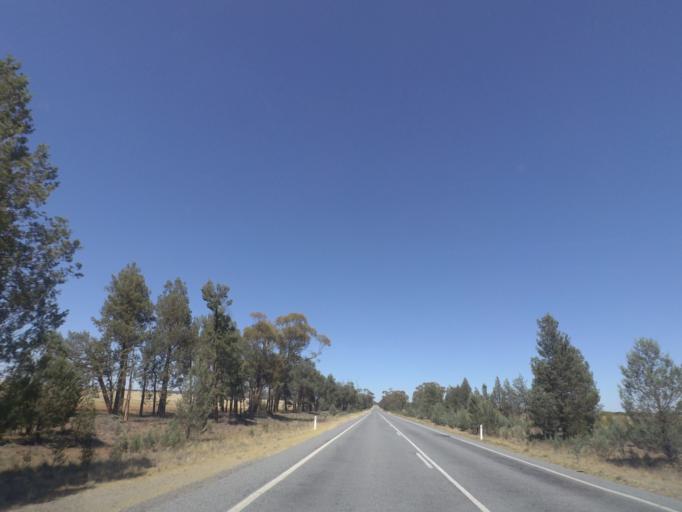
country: AU
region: New South Wales
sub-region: Narrandera
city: Narrandera
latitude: -34.4145
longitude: 146.8642
